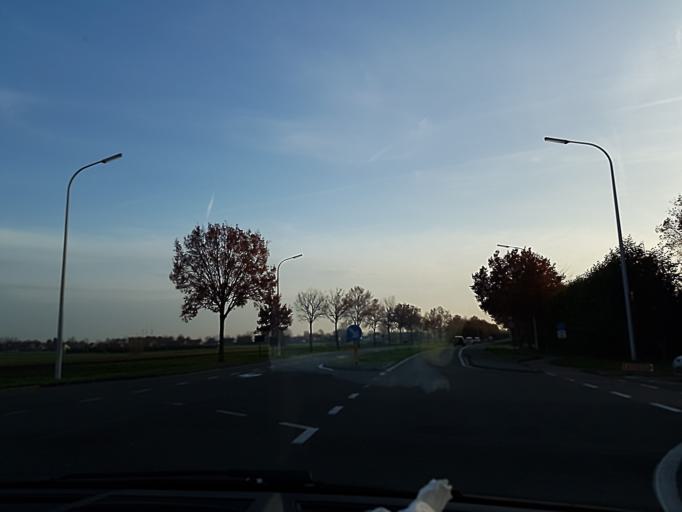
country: BE
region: Flanders
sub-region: Provincie Antwerpen
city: Essen
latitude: 51.4718
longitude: 4.4774
